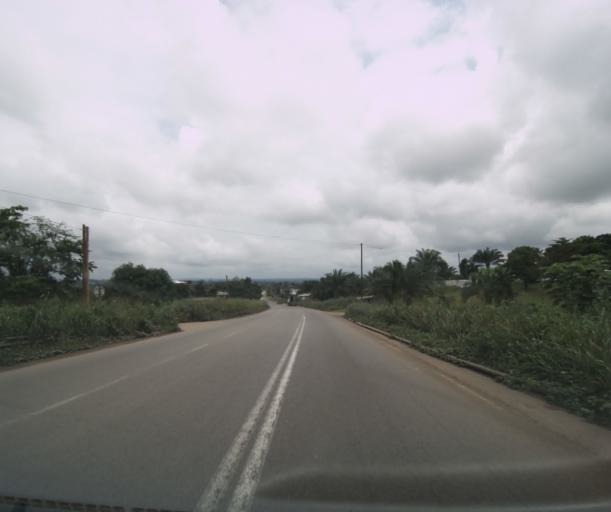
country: CM
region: Littoral
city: Edea
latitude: 3.7857
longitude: 10.1499
